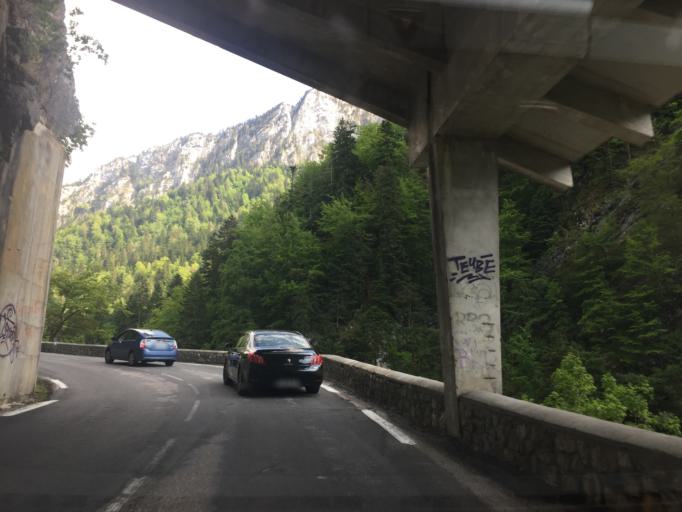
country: FR
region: Rhone-Alpes
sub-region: Departement de l'Isere
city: Saint-Laurent-du-Pont
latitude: 45.3493
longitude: 5.7792
